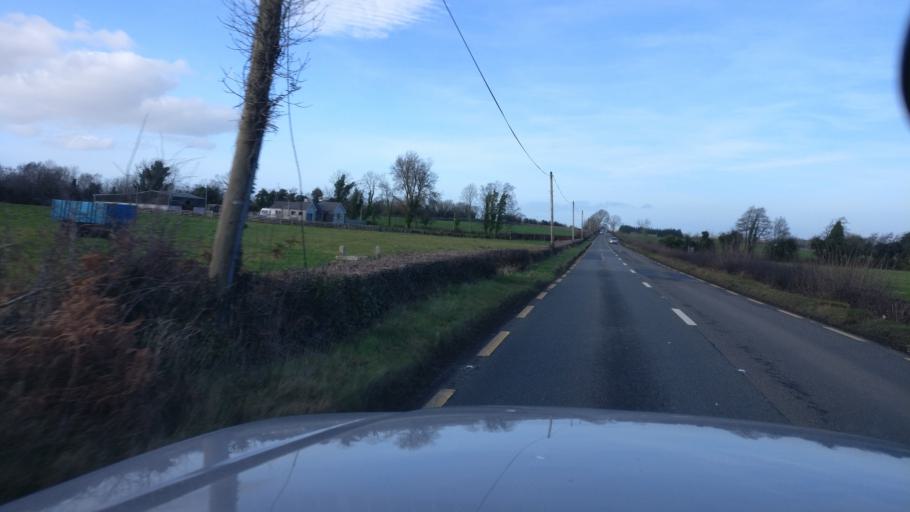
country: IE
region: Leinster
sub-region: Laois
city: Mountmellick
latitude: 53.0934
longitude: -7.3363
